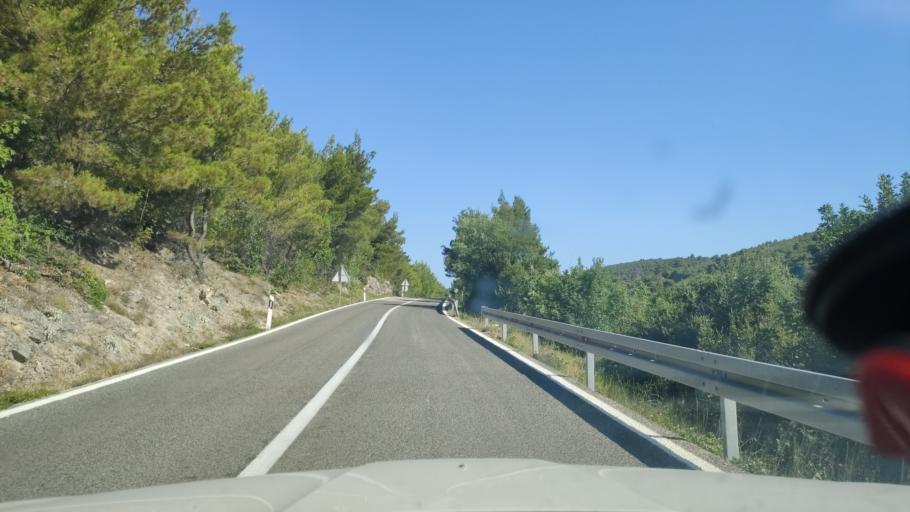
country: HR
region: Sibensko-Kniniska
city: Zaton
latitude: 43.8569
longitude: 15.8949
